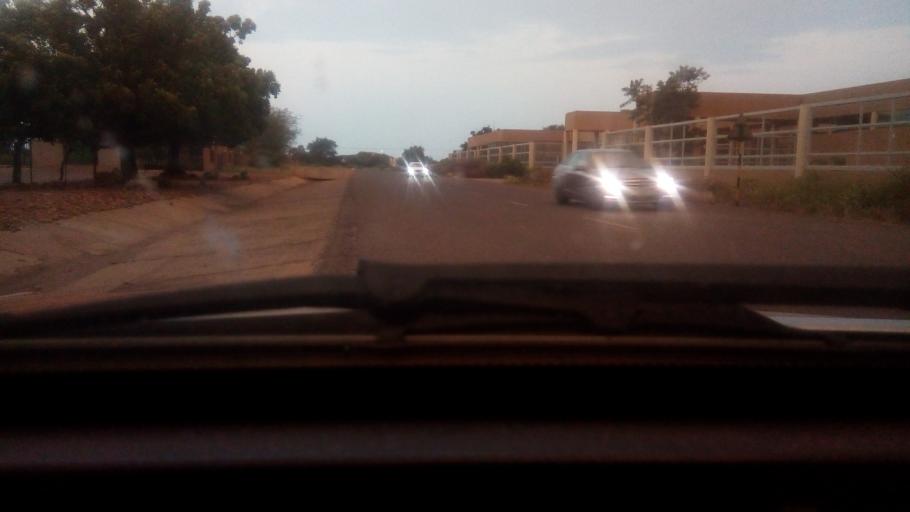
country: BW
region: Kweneng
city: Mmopone
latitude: -24.5909
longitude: 25.9153
